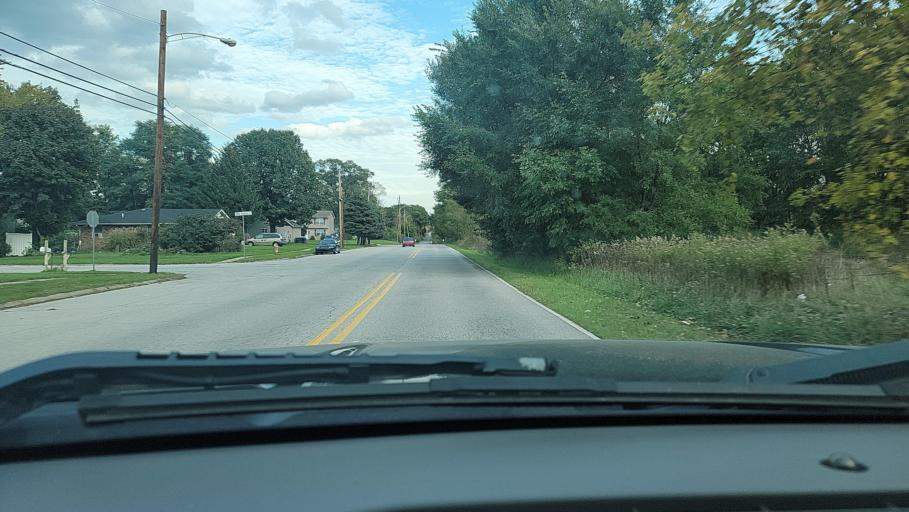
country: US
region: Indiana
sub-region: Porter County
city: Burns Harbor
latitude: 41.5958
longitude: -87.1476
